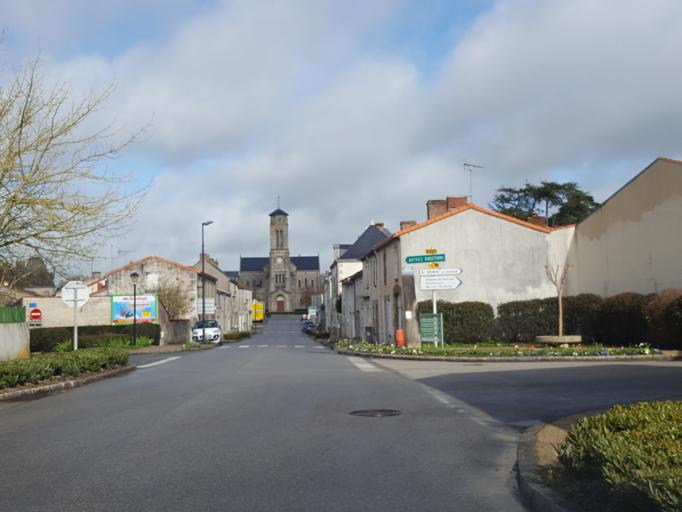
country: FR
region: Pays de la Loire
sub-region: Departement de la Vendee
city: Les Lucs-sur-Boulogne
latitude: 46.8414
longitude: -1.4924
